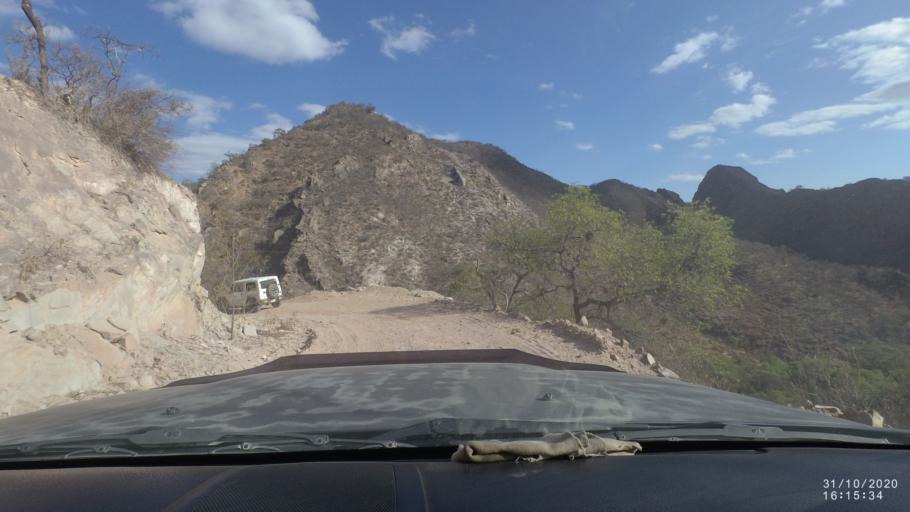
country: BO
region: Chuquisaca
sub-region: Provincia Zudanez
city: Mojocoya
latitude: -18.3889
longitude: -64.6123
